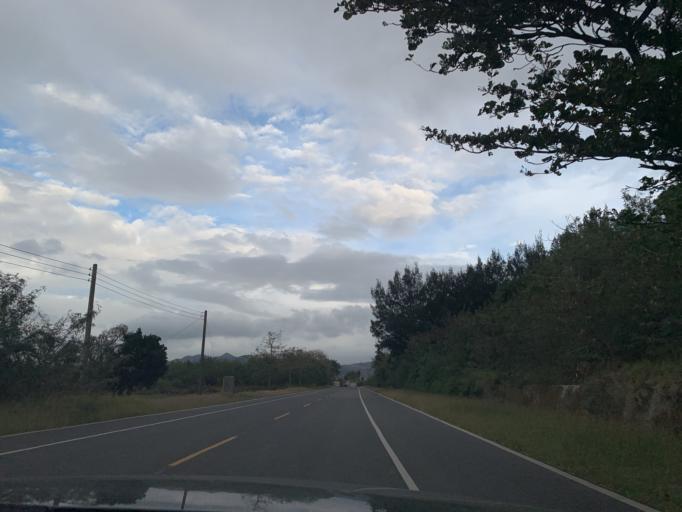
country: TW
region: Taiwan
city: Hengchun
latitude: 22.0500
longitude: 120.7086
